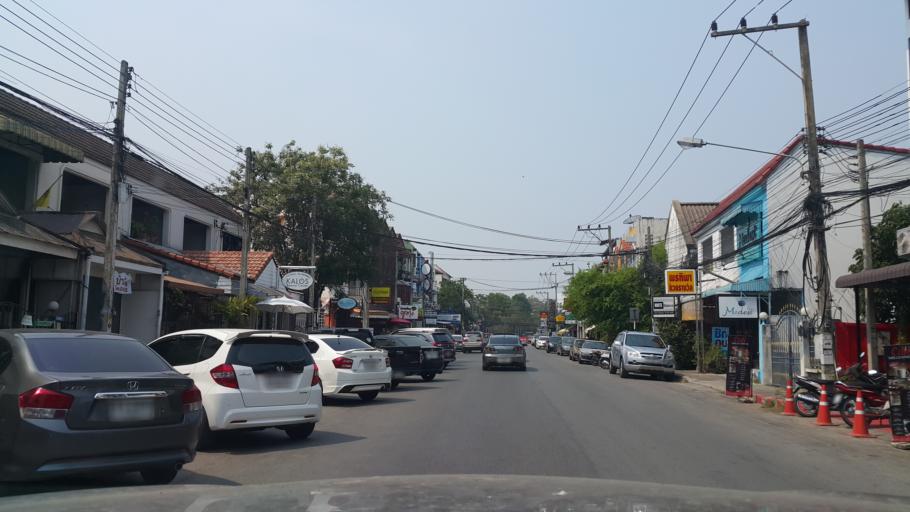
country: TH
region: Chiang Mai
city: Chiang Mai
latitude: 18.7884
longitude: 98.9625
